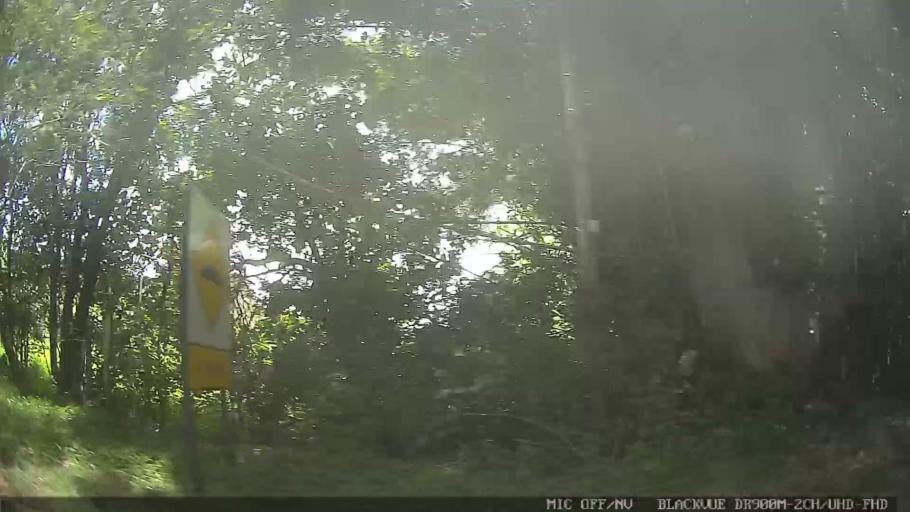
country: BR
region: Sao Paulo
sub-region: Braganca Paulista
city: Braganca Paulista
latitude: -22.9861
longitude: -46.4791
